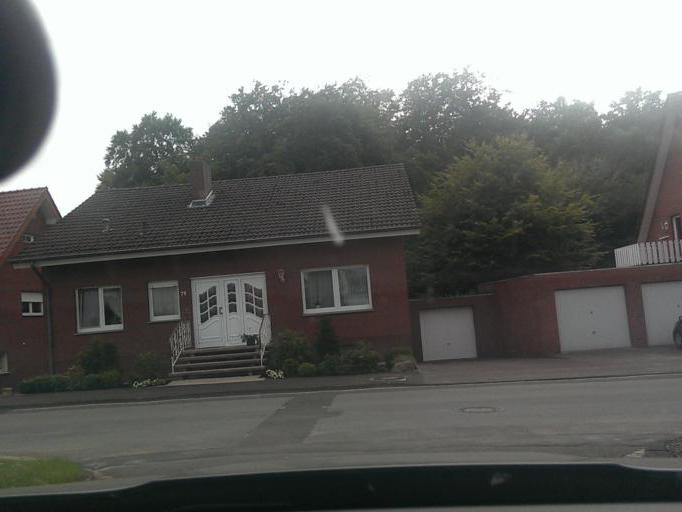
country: DE
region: North Rhine-Westphalia
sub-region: Regierungsbezirk Detmold
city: Delbruck
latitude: 51.7724
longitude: 8.5558
